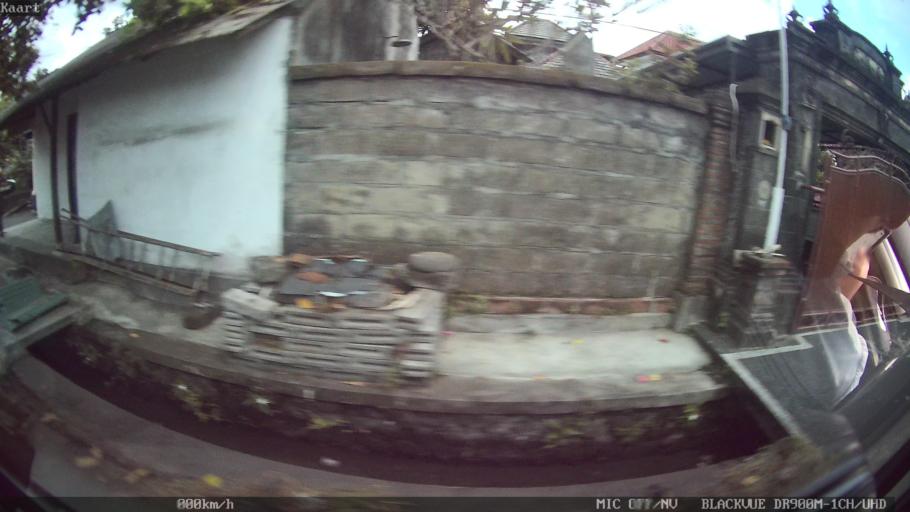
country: ID
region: Bali
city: Banjar Bucu
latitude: -8.5917
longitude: 115.2064
